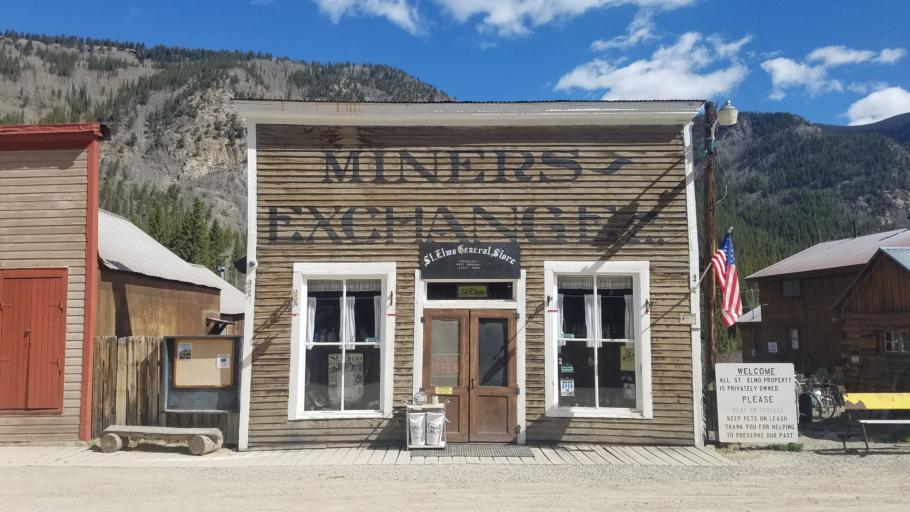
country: US
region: Colorado
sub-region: Chaffee County
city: Buena Vista
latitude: 38.7037
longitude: -106.3455
